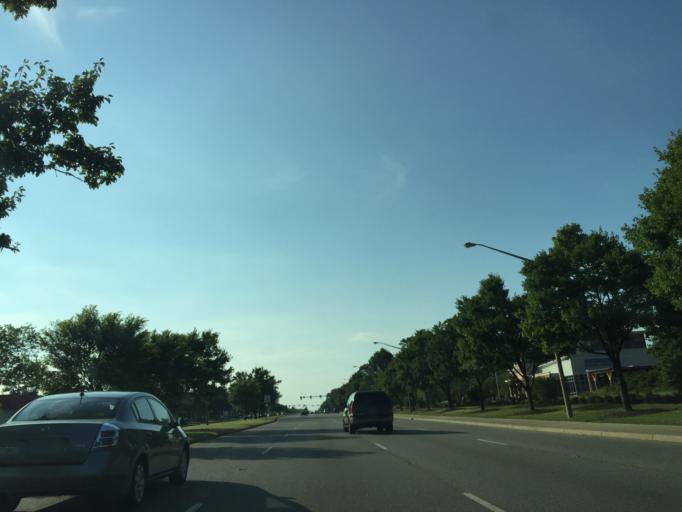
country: US
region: Virginia
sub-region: York County
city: Yorktown
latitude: 37.1243
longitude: -76.5087
